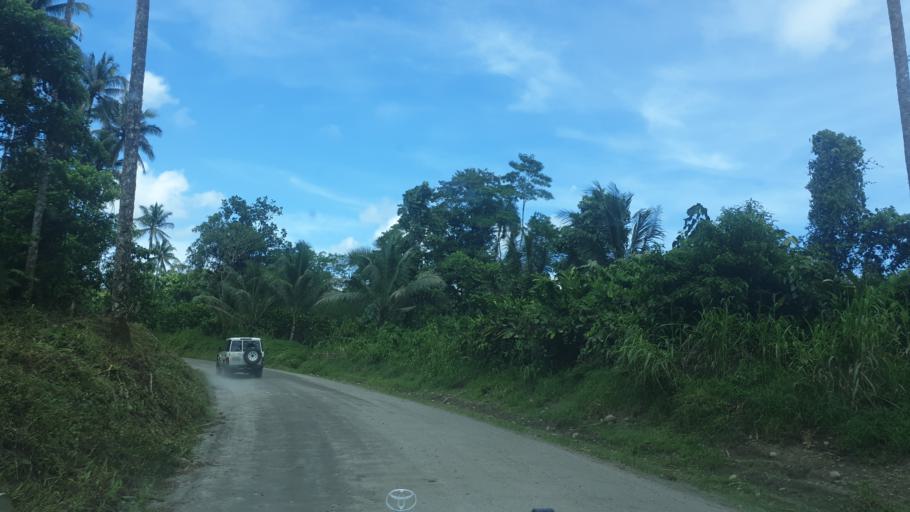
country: PG
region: Bougainville
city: Panguna
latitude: -6.7387
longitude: 155.6625
